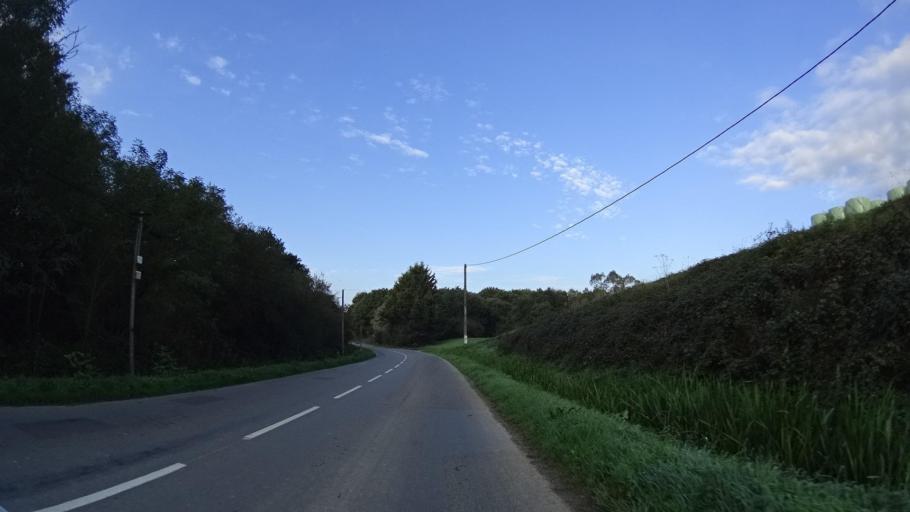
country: FR
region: Brittany
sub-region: Departement des Cotes-d'Armor
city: Plouasne
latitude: 48.2751
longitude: -2.0309
